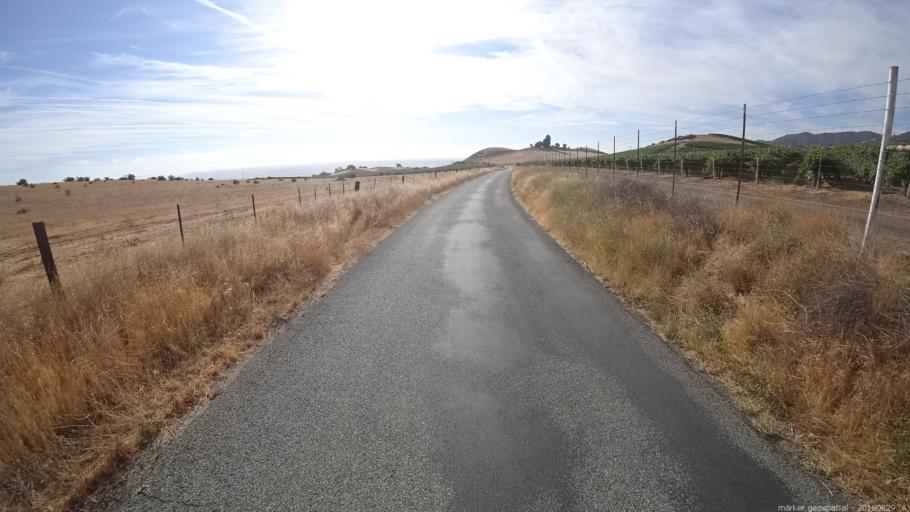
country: US
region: California
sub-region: Monterey County
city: King City
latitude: 36.0180
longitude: -120.9435
